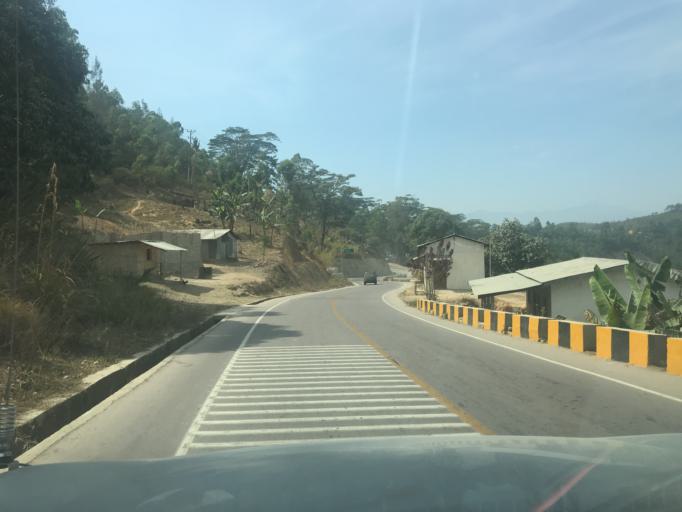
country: TL
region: Aileu
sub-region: Aileu Villa
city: Aileu
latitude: -8.6751
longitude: 125.5505
